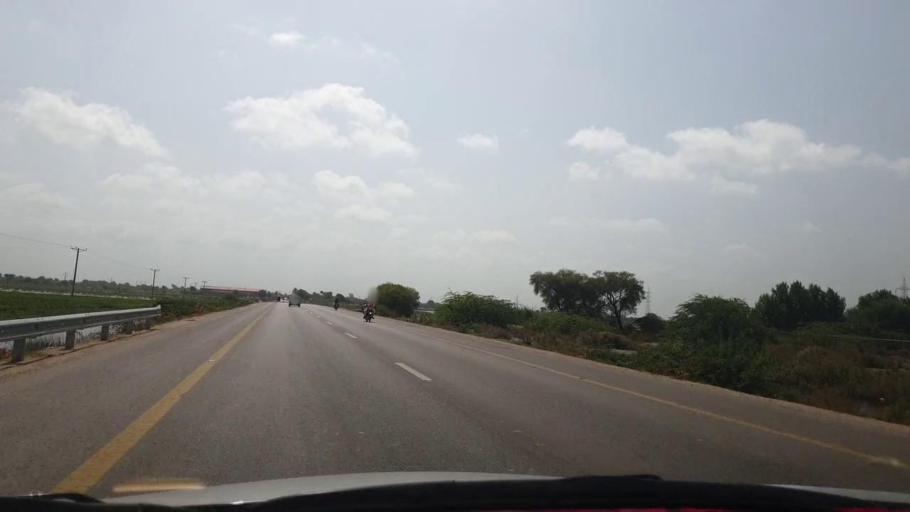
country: PK
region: Sindh
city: Talhar
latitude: 24.9175
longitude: 68.7261
